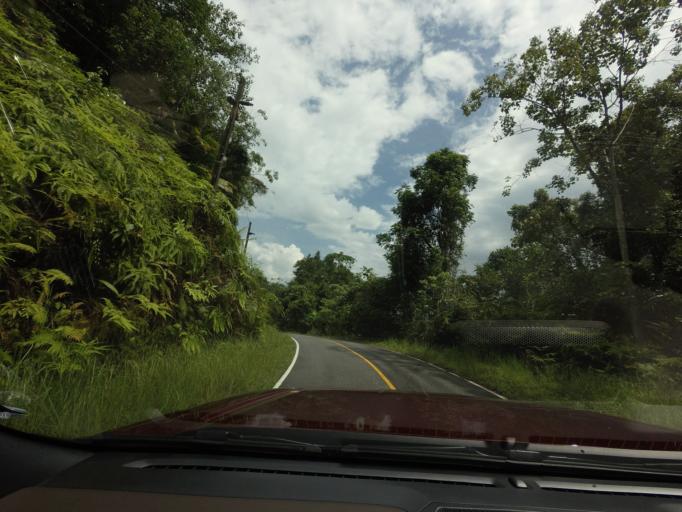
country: TH
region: Narathiwat
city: Sukhirin
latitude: 5.9428
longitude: 101.6525
